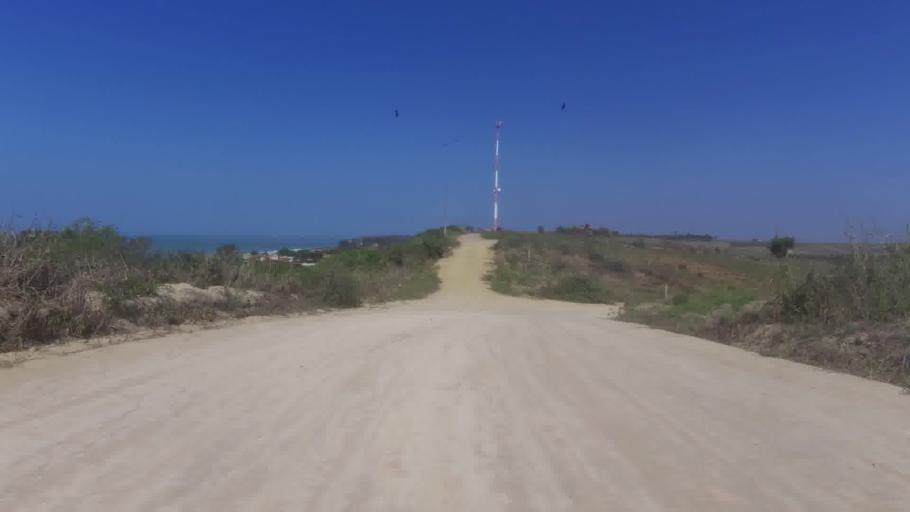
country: BR
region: Espirito Santo
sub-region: Marataizes
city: Marataizes
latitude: -21.1022
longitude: -40.8510
